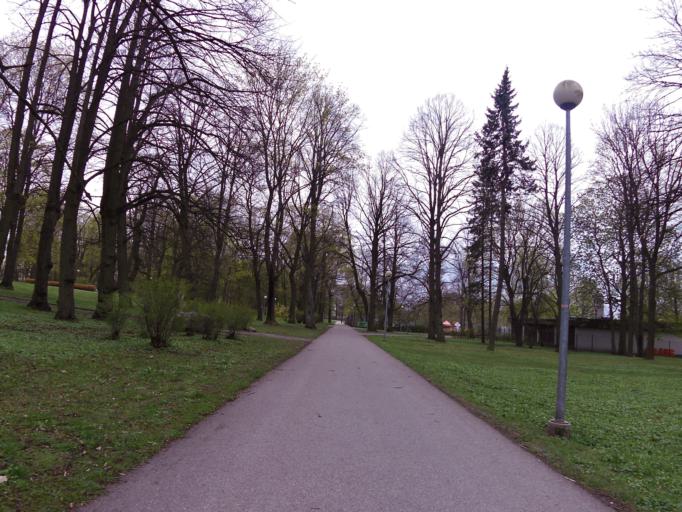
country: EE
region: Harju
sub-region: Tallinna linn
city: Tallinn
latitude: 59.4542
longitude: 24.6821
